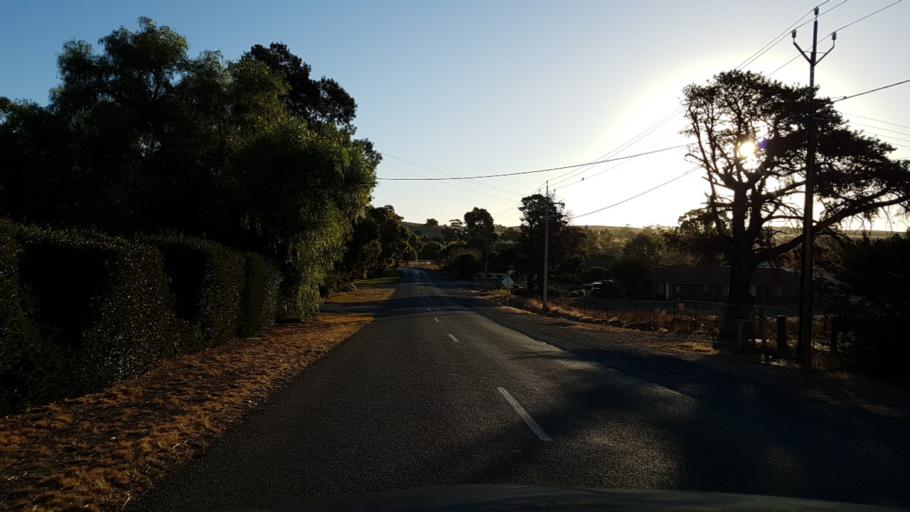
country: AU
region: South Australia
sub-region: Clare and Gilbert Valleys
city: Clare
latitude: -34.0226
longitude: 138.6902
